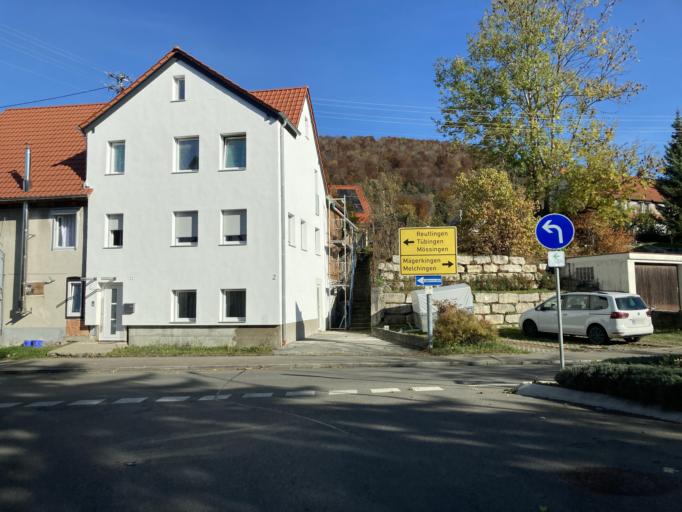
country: DE
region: Baden-Wuerttemberg
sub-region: Tuebingen Region
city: Mossingen
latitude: 48.3803
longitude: 9.1085
